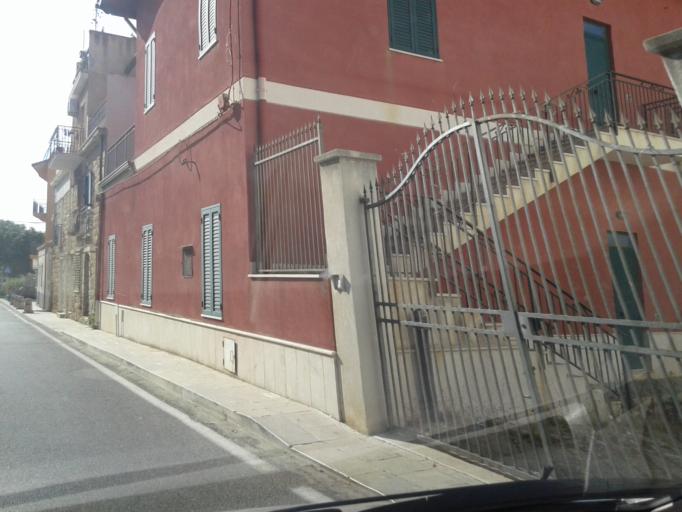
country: IT
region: Sicily
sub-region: Palermo
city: Finale
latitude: 38.0199
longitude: 14.1635
